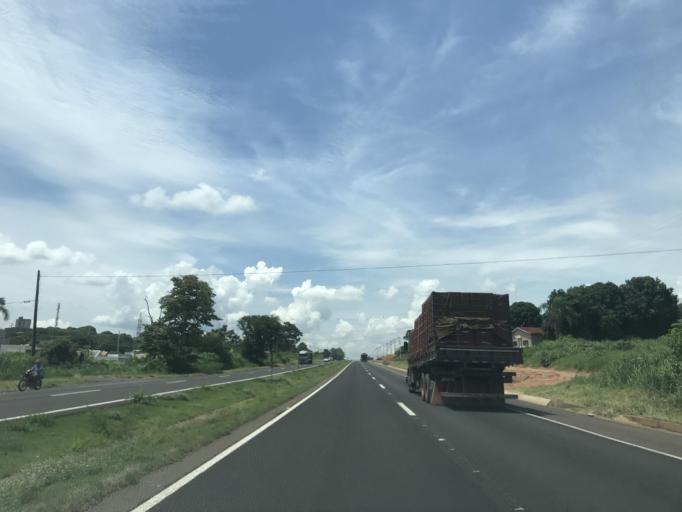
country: BR
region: Parana
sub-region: Alto Parana
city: Alto Parana
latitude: -23.1844
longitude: -52.2133
